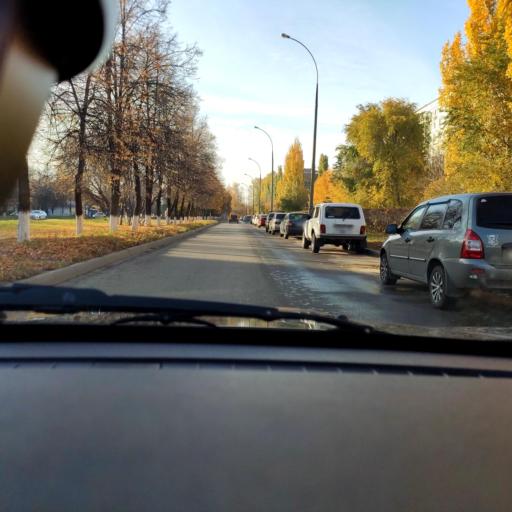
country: RU
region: Samara
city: Tol'yatti
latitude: 53.5212
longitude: 49.3102
